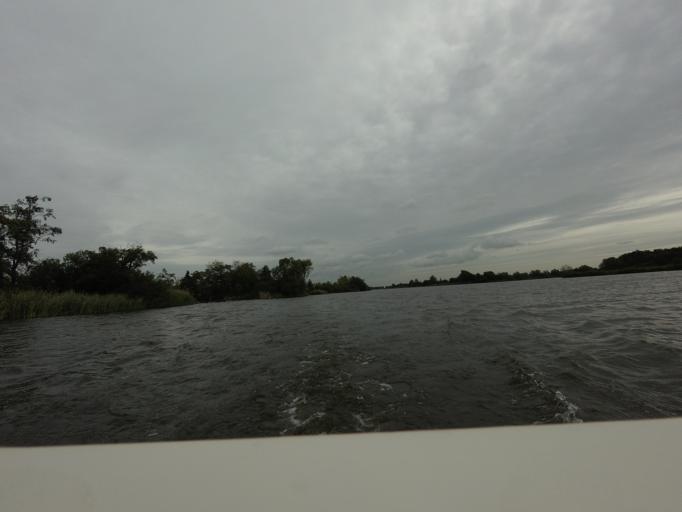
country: NL
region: Friesland
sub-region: Gemeente Boarnsterhim
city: Warten
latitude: 53.1214
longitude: 5.9072
